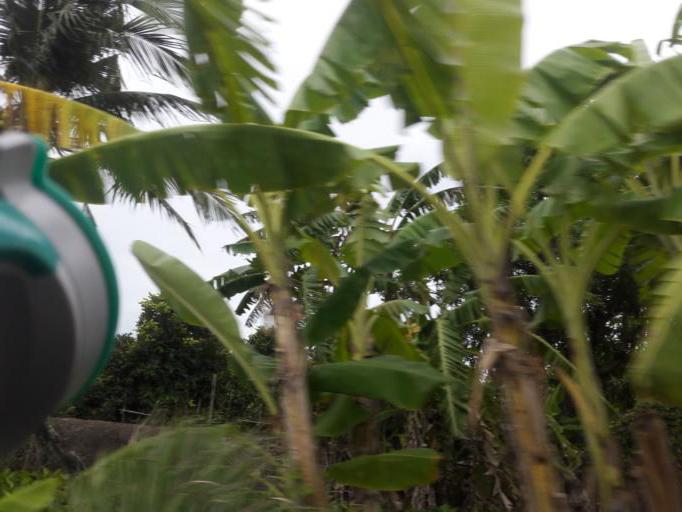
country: TH
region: Ratchaburi
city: Damnoen Saduak
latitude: 13.5326
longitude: 100.0098
